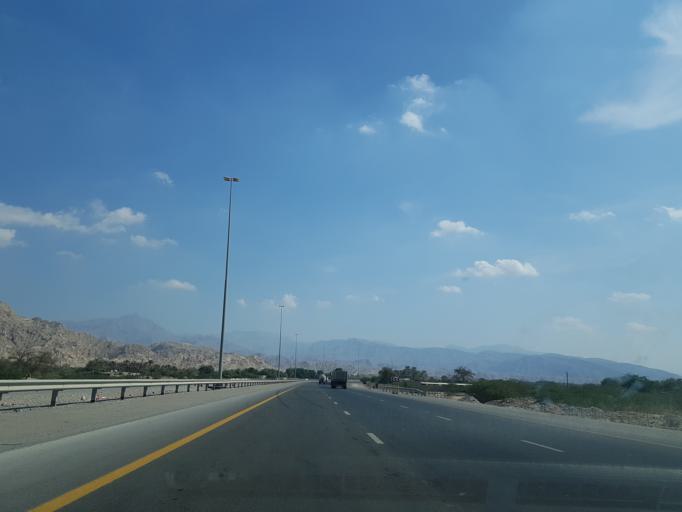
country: AE
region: Ra's al Khaymah
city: Ras al-Khaimah
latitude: 25.8281
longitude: 56.0189
